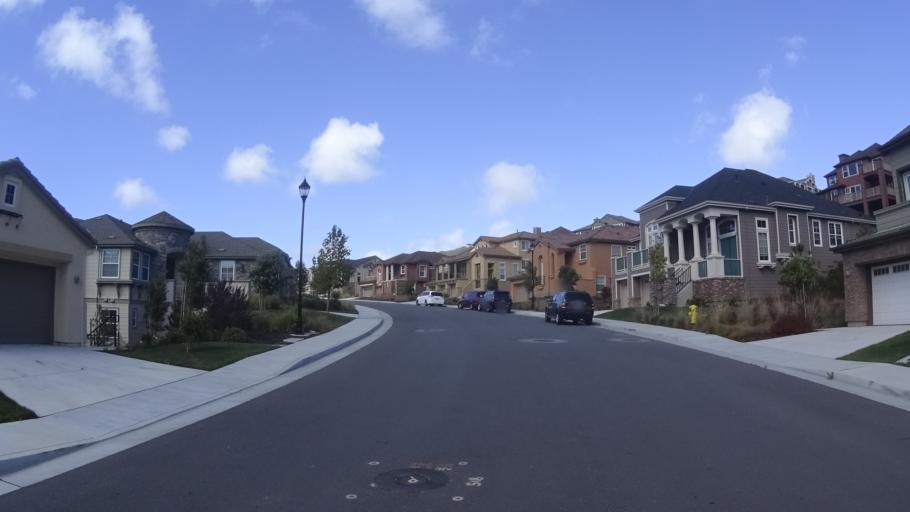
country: US
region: California
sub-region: San Mateo County
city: Brisbane
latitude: 37.6962
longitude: -122.4179
